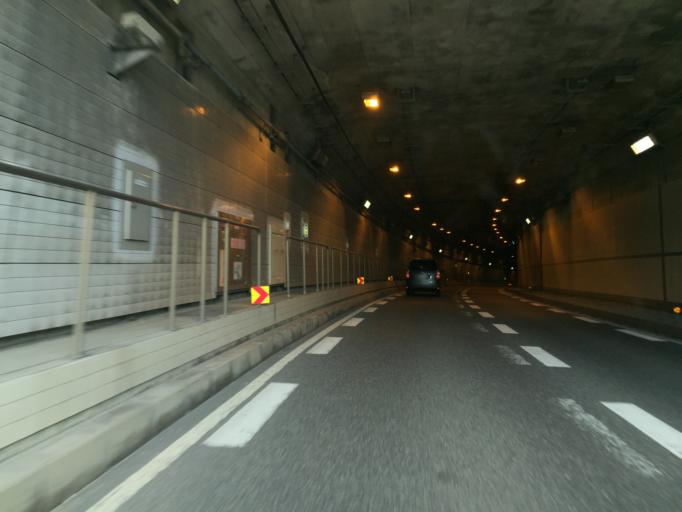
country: JP
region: Niigata
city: Niigata-shi
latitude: 37.9429
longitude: 139.0589
